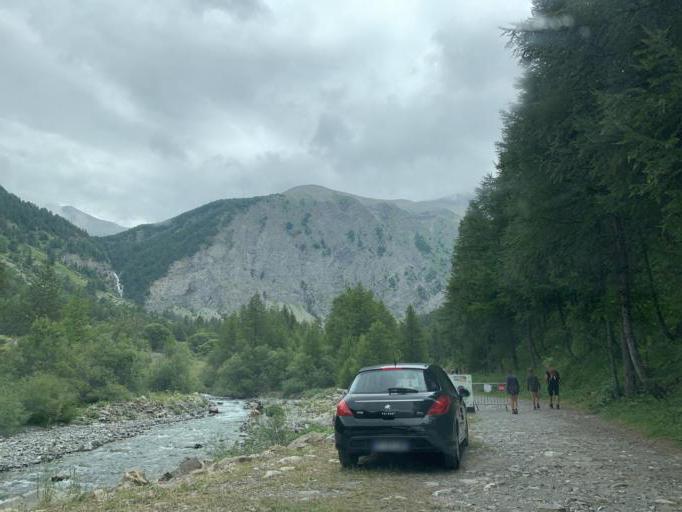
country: FR
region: Provence-Alpes-Cote d'Azur
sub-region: Departement des Hautes-Alpes
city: Guillestre
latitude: 44.5442
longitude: 6.6335
